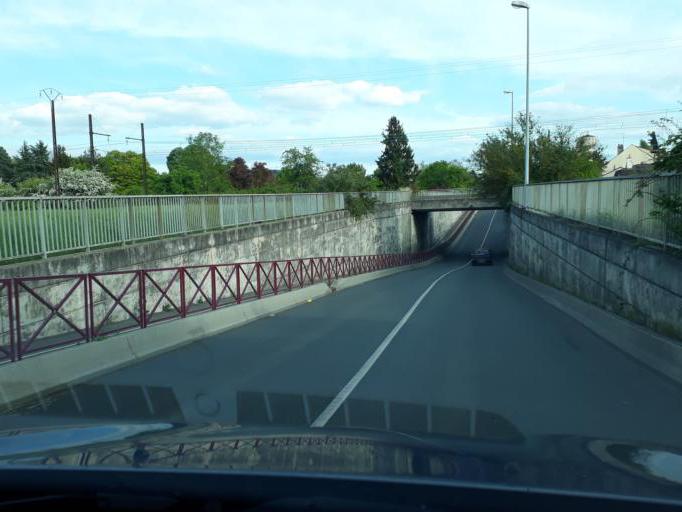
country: FR
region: Centre
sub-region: Departement du Loiret
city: La Chapelle-Saint-Mesmin
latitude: 47.8971
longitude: 1.8364
